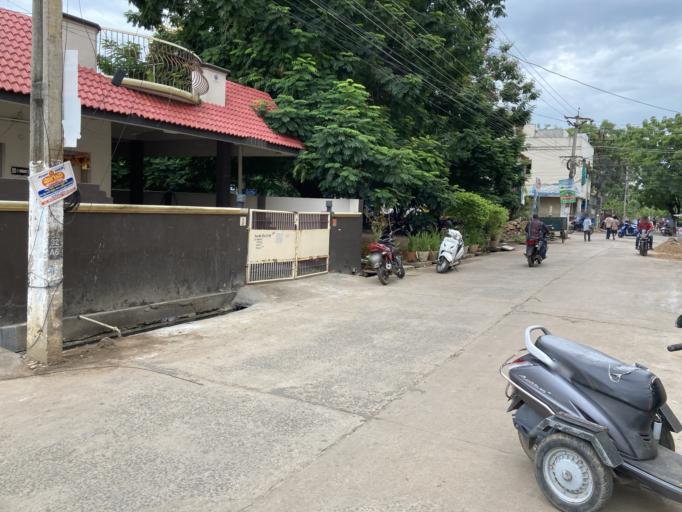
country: IN
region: Andhra Pradesh
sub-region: West Godavari
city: Eluru
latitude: 16.7141
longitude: 81.0985
